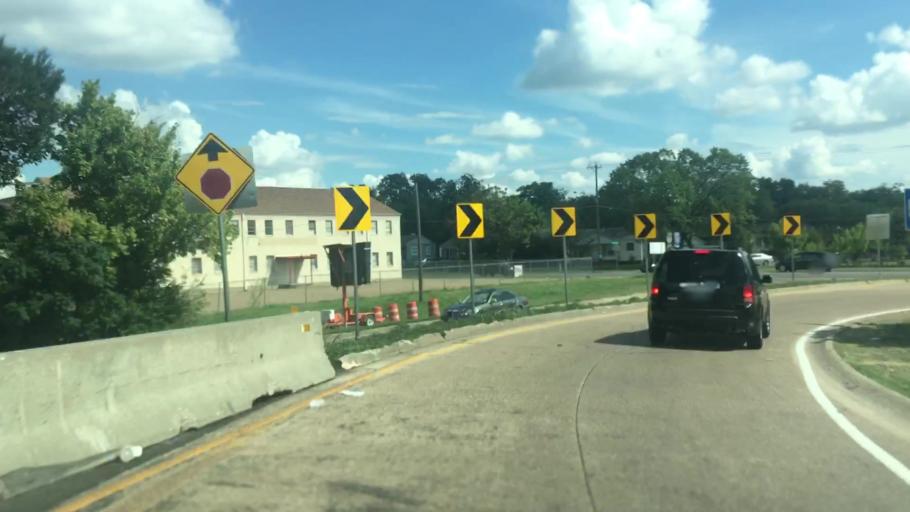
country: US
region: Texas
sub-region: Dallas County
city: Cockrell Hill
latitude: 32.7139
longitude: -96.8285
